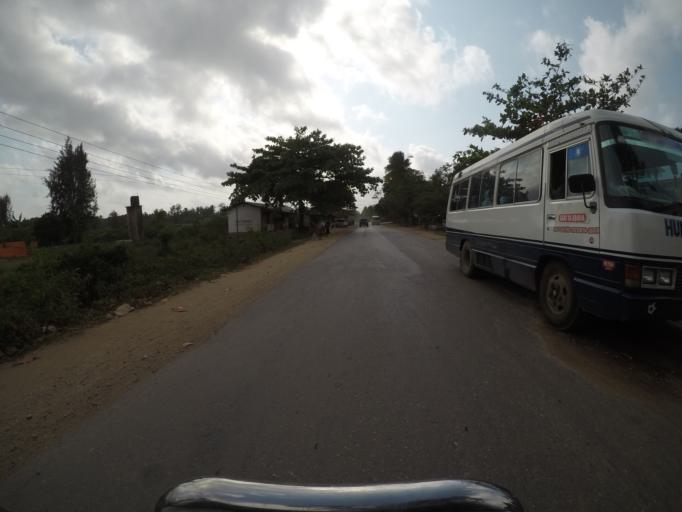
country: TZ
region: Zanzibar Central/South
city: Koani
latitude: -6.1957
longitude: 39.2805
